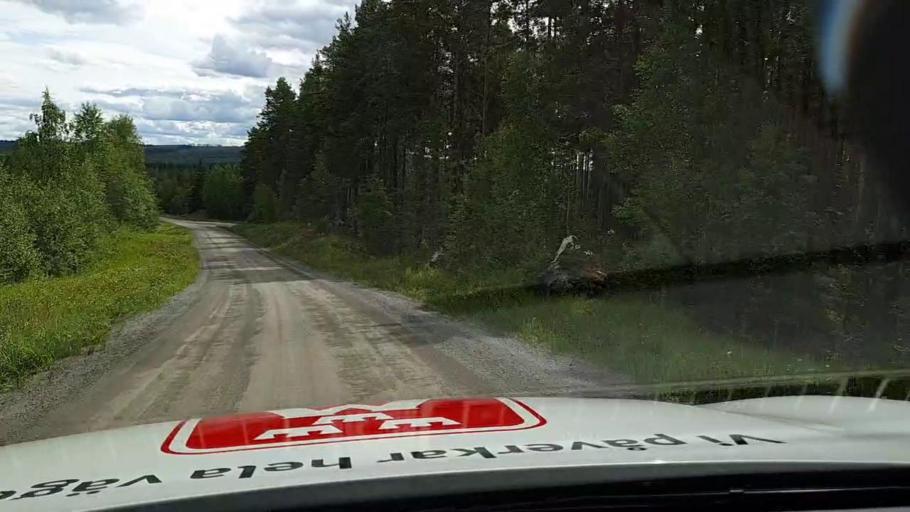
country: SE
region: Jaemtland
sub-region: Braecke Kommun
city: Braecke
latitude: 63.2232
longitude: 15.3450
